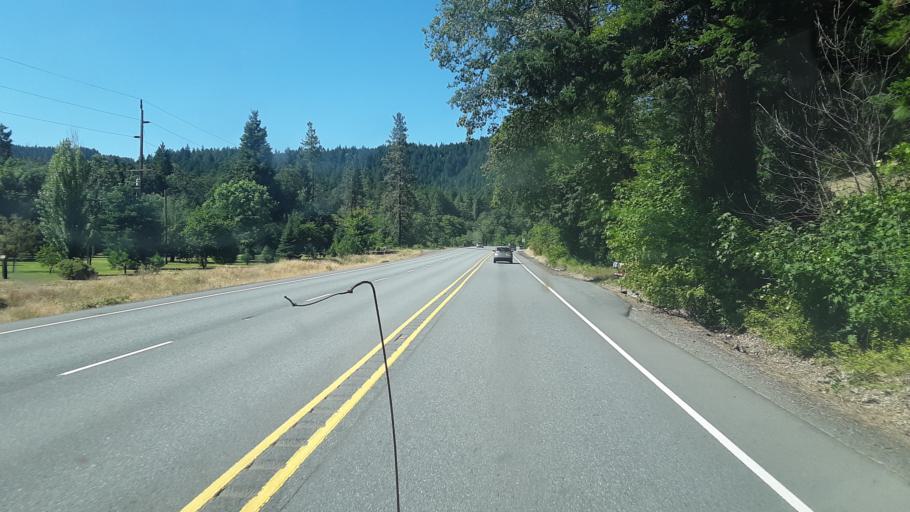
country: US
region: Oregon
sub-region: Josephine County
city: Redwood
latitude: 42.3676
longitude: -123.5076
